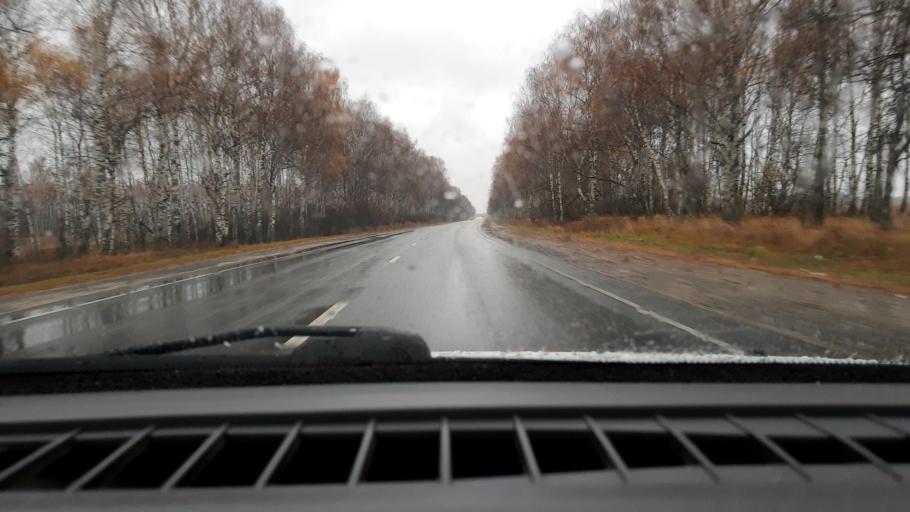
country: RU
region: Nizjnij Novgorod
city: Sitniki
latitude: 56.5104
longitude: 44.0236
